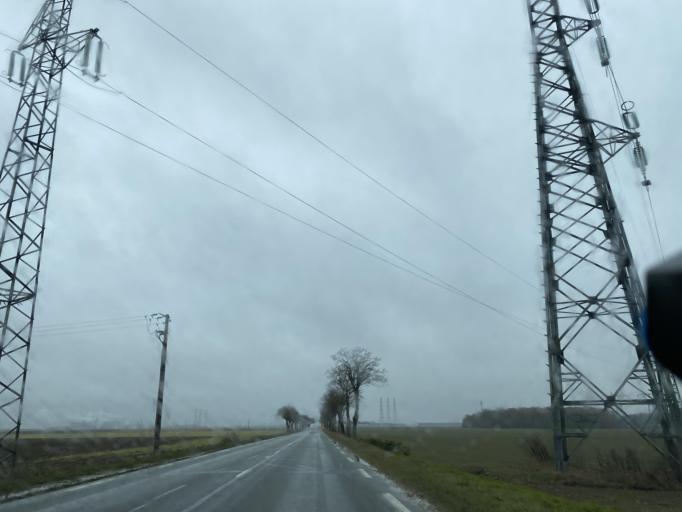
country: FR
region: Centre
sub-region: Departement du Loiret
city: Artenay
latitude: 48.1140
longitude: 1.8606
